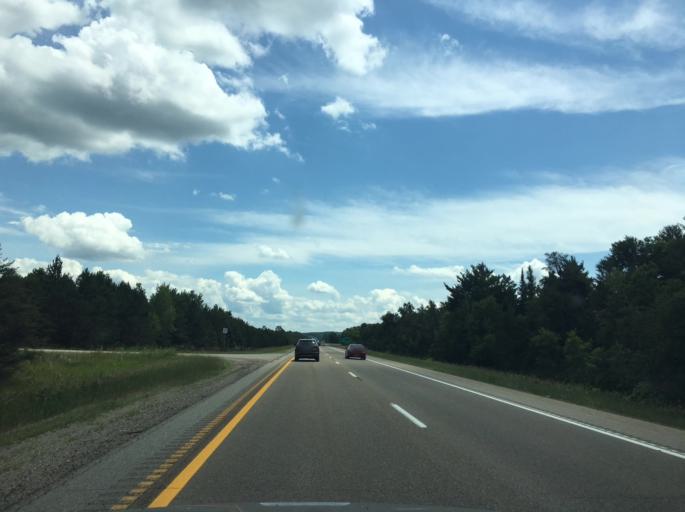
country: US
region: Michigan
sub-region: Roscommon County
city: Roscommon
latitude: 44.5210
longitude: -84.6693
